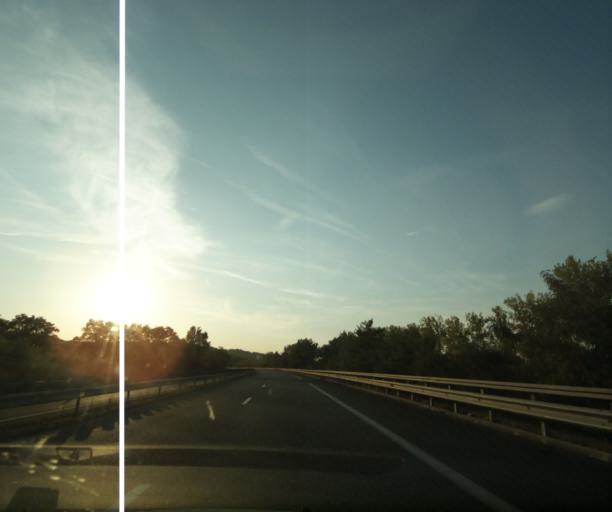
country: FR
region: Aquitaine
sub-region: Departement du Lot-et-Garonne
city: Layrac
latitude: 44.1421
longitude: 0.6631
